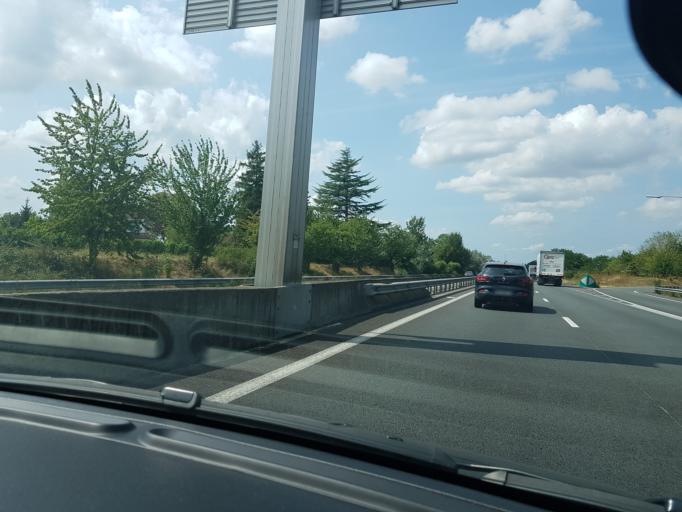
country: FR
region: Aquitaine
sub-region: Departement de la Gironde
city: Vayres
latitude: 44.8818
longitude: -0.3119
